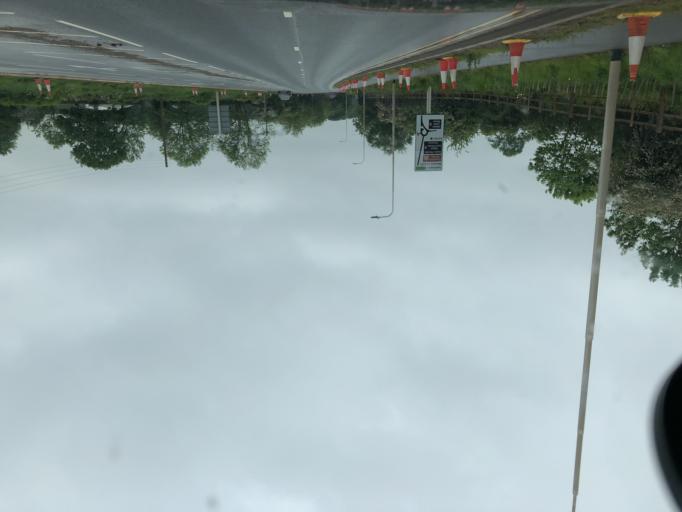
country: GB
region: England
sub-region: Warwickshire
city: Harbury
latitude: 52.1923
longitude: -1.4759
